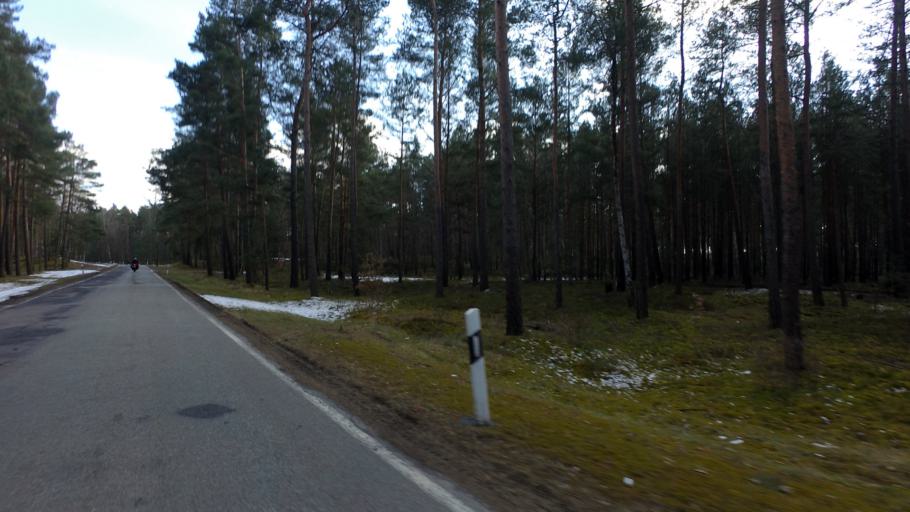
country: DE
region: Brandenburg
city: Marienwerder
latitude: 52.8013
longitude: 13.5912
